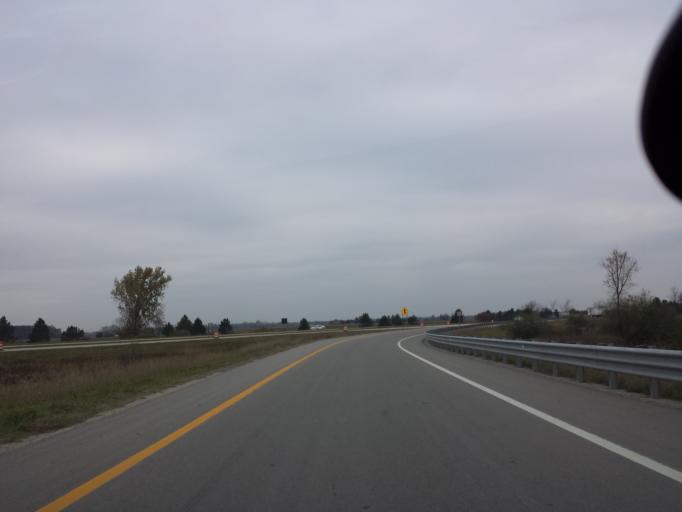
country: US
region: Michigan
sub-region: Bay County
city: Pinconning
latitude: 43.8565
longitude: -84.0193
